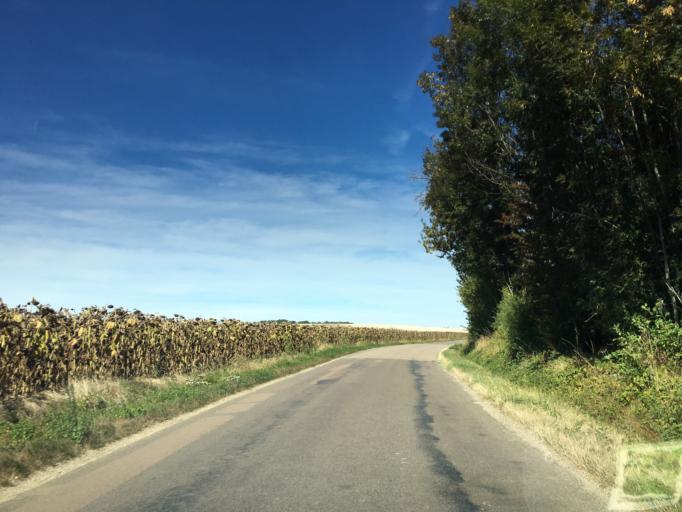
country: FR
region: Bourgogne
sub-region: Departement de l'Yonne
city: Fleury-la-Vallee
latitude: 47.8640
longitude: 3.4401
